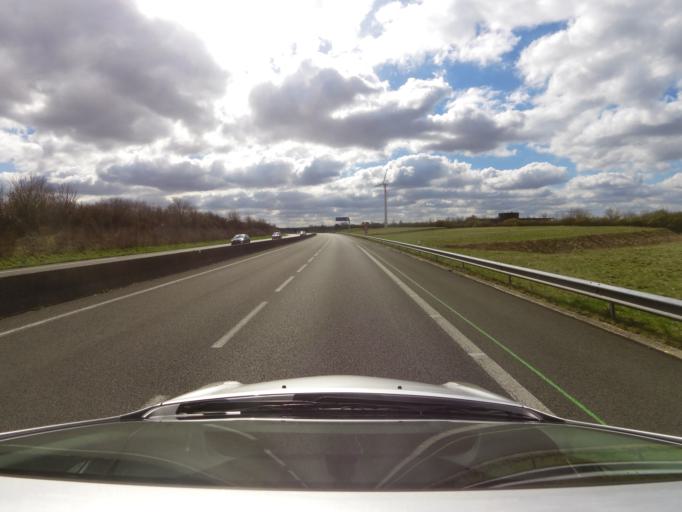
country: FR
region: Picardie
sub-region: Departement de la Somme
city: Sailly-Flibeaucourt
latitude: 50.1714
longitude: 1.7547
